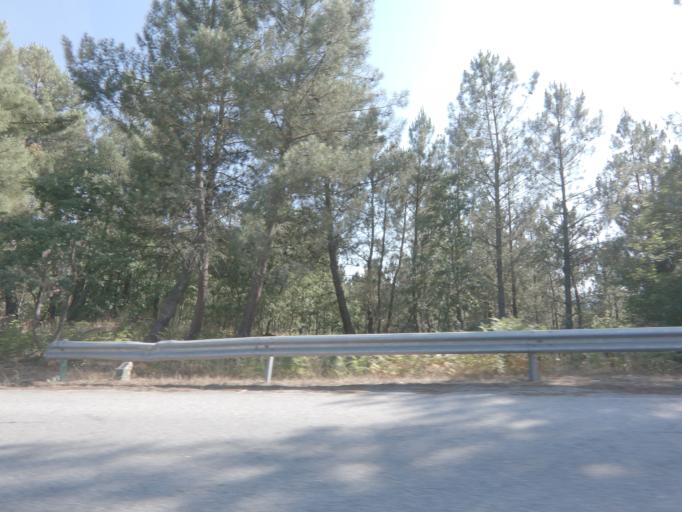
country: PT
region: Viseu
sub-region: Moimenta da Beira
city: Moimenta da Beira
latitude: 40.9759
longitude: -7.5779
